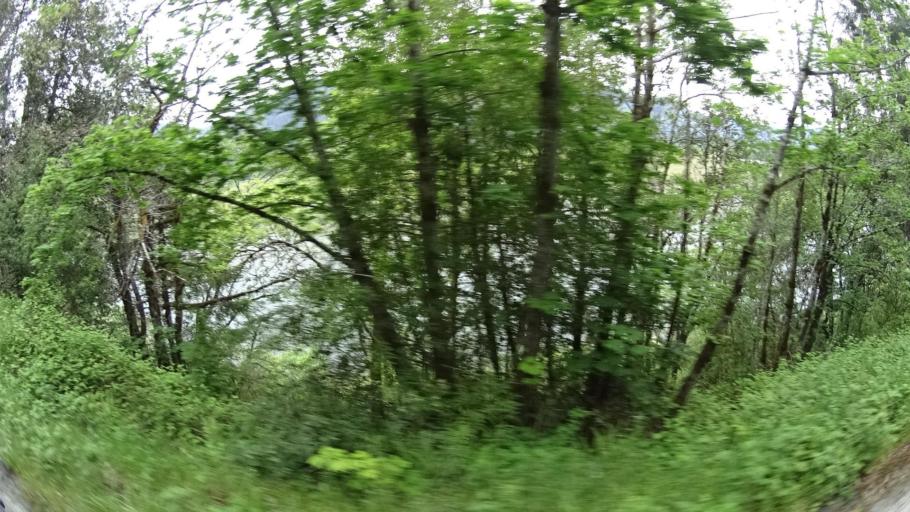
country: US
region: California
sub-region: Humboldt County
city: Willow Creek
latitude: 41.0660
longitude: -123.6951
